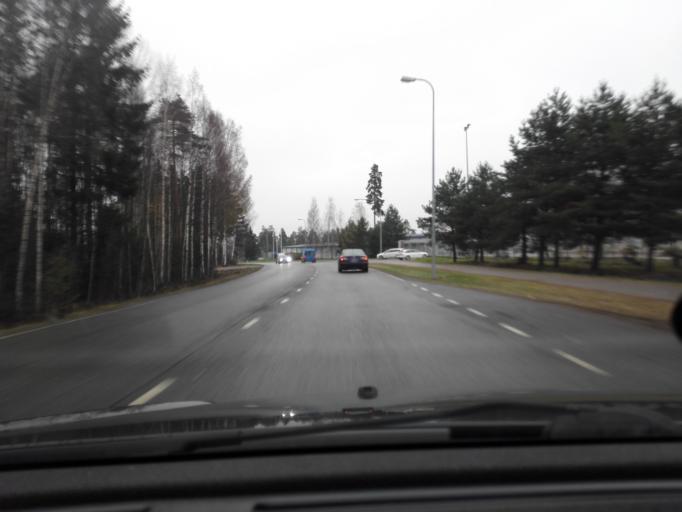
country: FI
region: Uusimaa
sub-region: Helsinki
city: Vantaa
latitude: 60.3046
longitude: 25.0933
